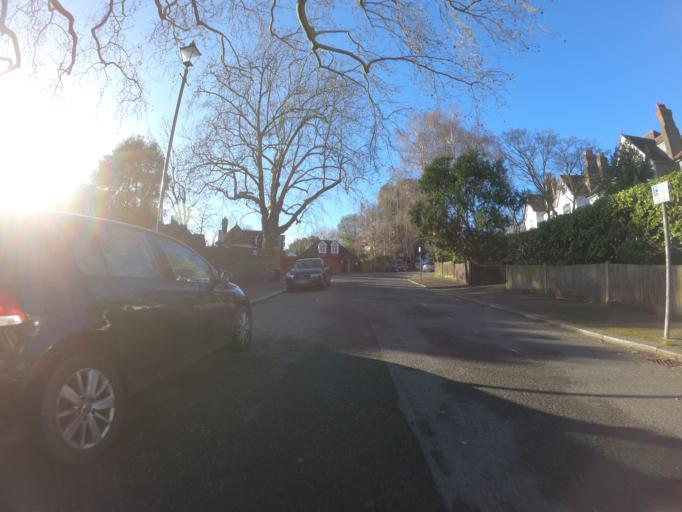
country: GB
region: England
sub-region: Greater London
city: Blackheath
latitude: 51.4677
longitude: -0.0010
